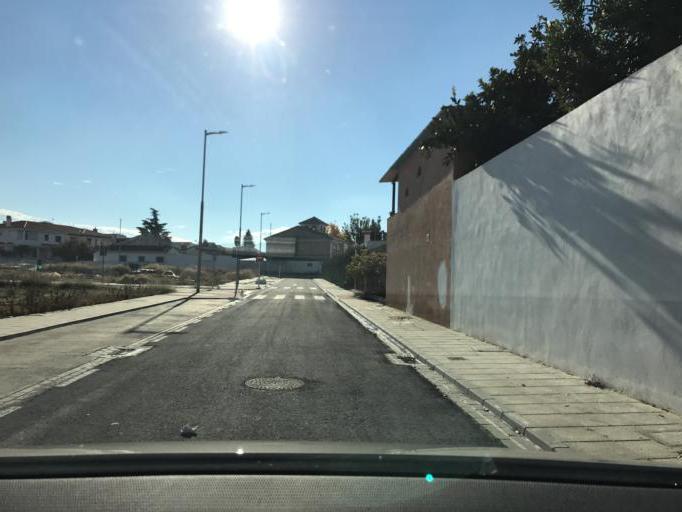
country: ES
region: Andalusia
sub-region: Provincia de Granada
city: Churriana de la Vega
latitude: 37.1496
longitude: -3.6539
